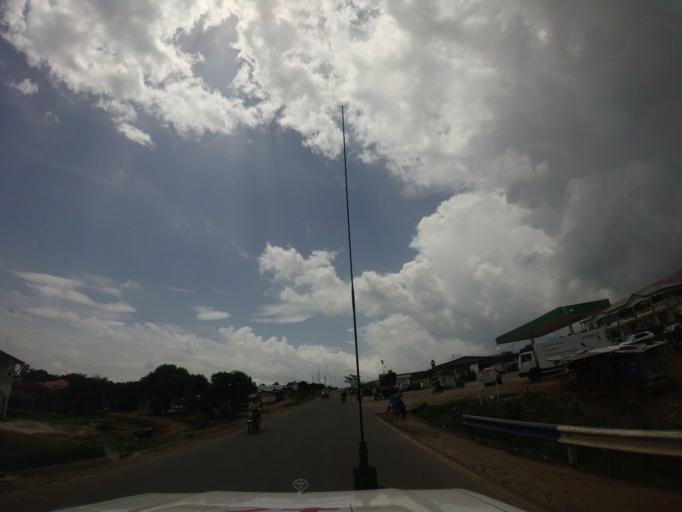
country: SL
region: Western Area
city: Waterloo
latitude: 8.3323
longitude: -13.0465
